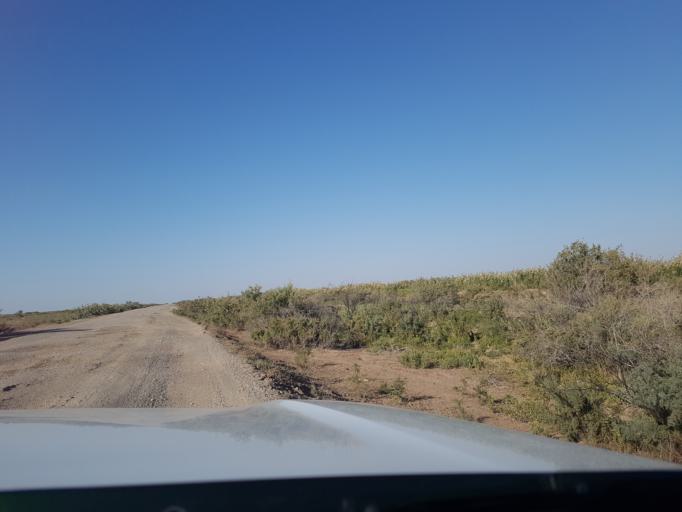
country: IR
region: Razavi Khorasan
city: Sarakhs
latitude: 36.9564
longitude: 61.3812
